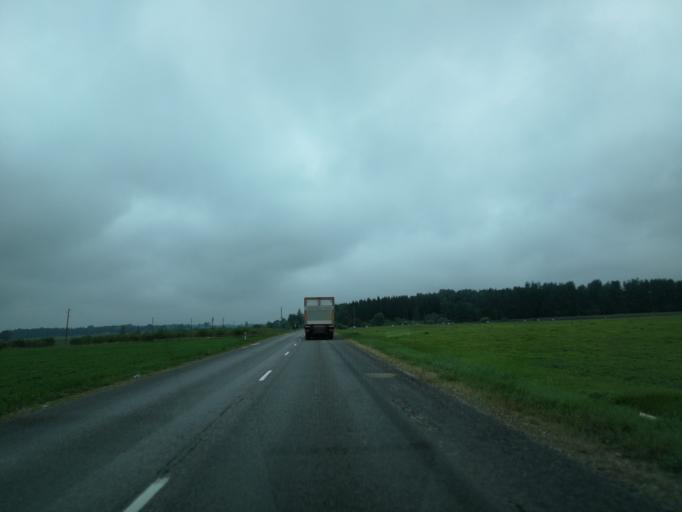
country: LV
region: Livani
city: Livani
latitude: 56.3483
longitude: 26.2729
